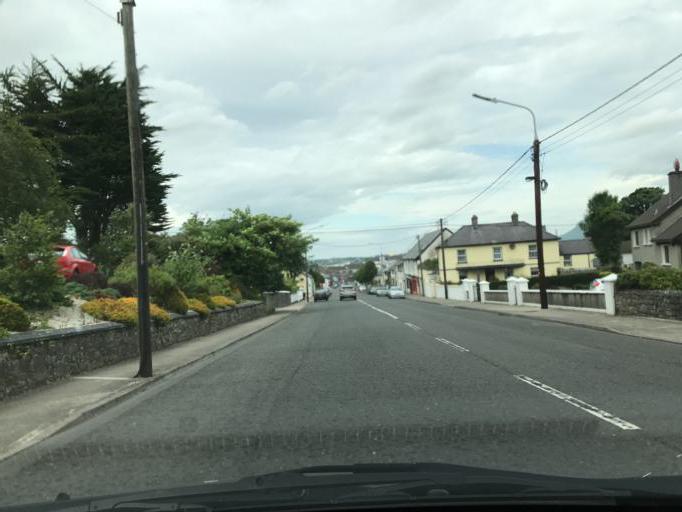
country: IE
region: Connaught
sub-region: Sligo
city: Sligo
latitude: 54.2637
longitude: -8.4696
